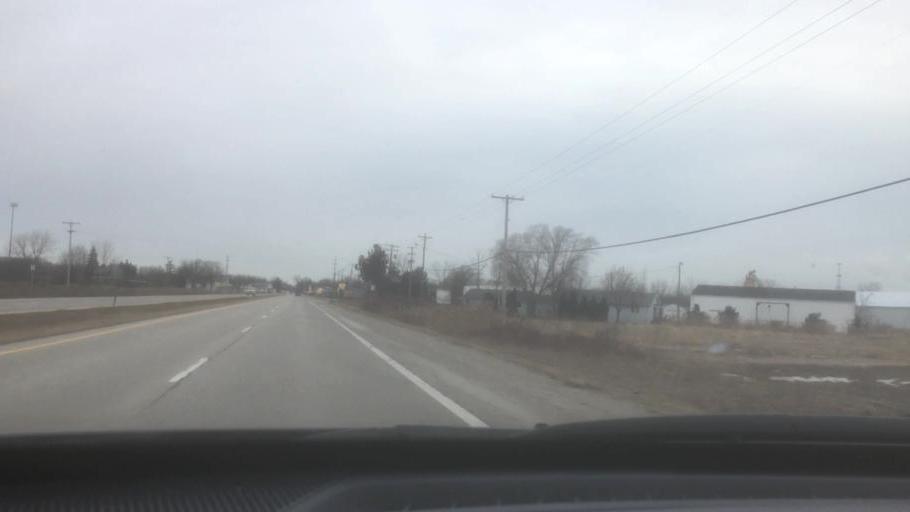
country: US
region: Michigan
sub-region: Bay County
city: Essexville
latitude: 43.5736
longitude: -83.8510
